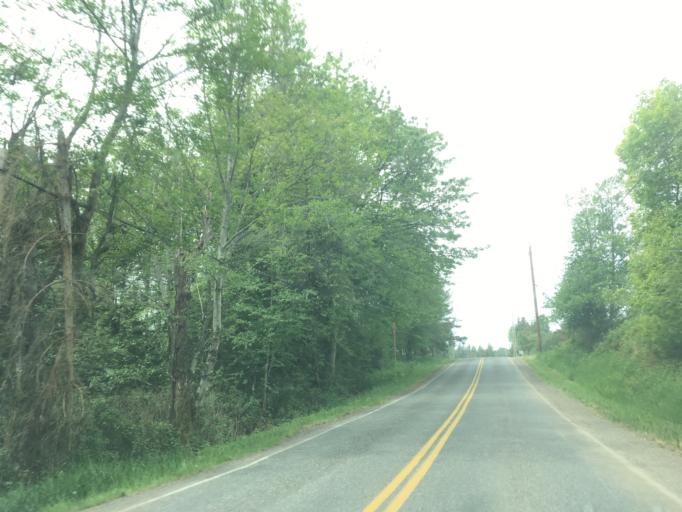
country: US
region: Washington
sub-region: Whatcom County
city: Bellingham
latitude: 48.8188
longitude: -122.4730
